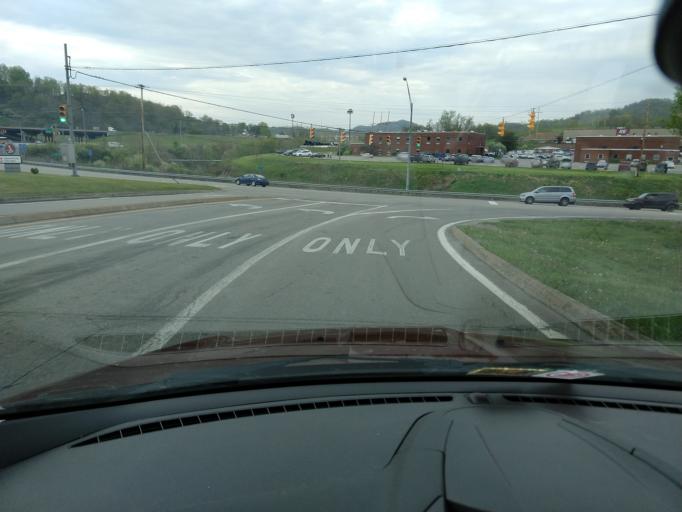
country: US
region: West Virginia
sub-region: Harrison County
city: Bridgeport
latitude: 39.3096
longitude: -80.2771
